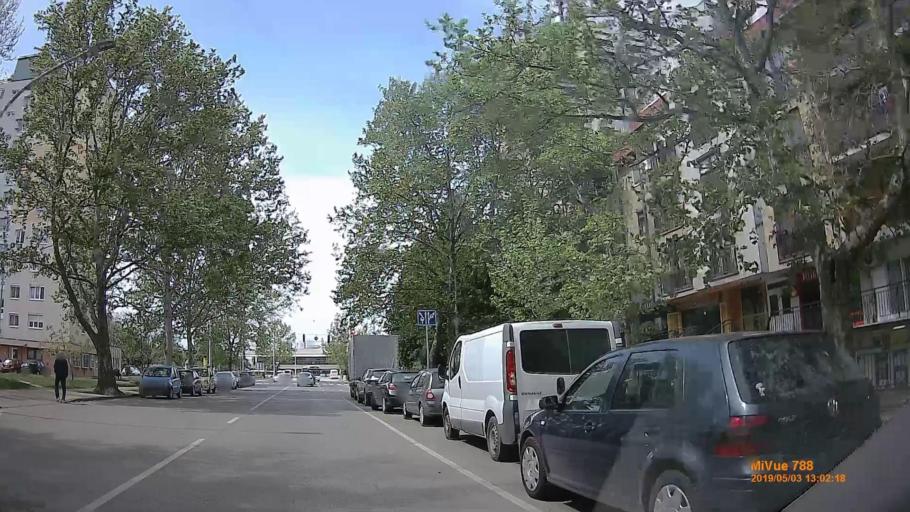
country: HU
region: Jasz-Nagykun-Szolnok
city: Szolnok
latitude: 47.1781
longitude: 20.1793
